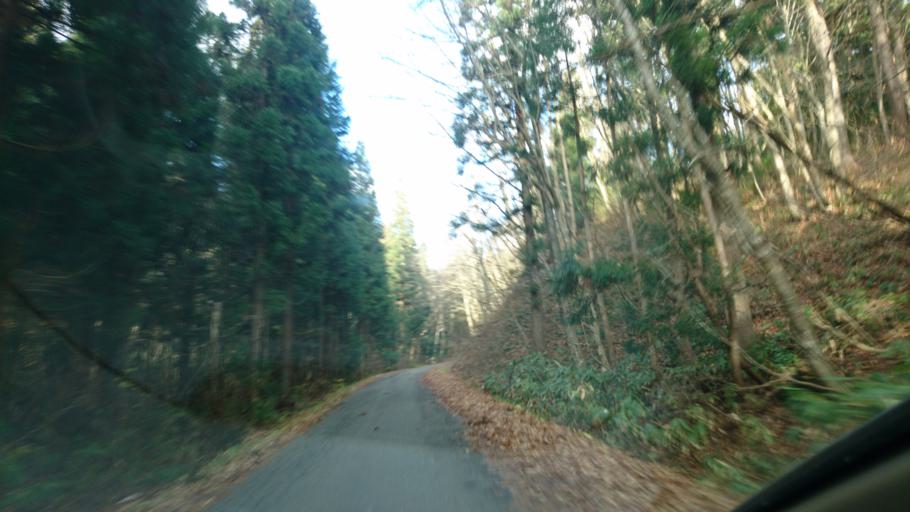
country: JP
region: Akita
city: Kakunodatemachi
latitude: 39.4649
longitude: 140.7894
